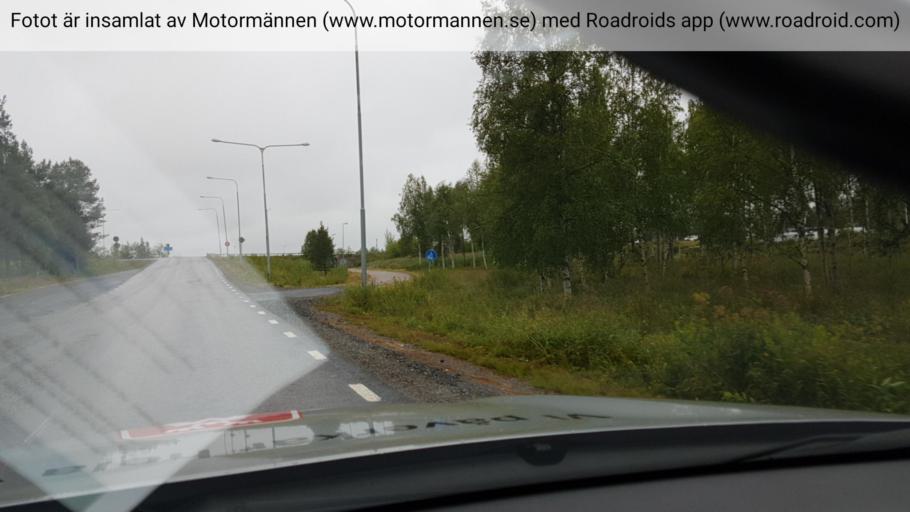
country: SE
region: Norrbotten
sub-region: Gallivare Kommun
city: Gaellivare
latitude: 67.1263
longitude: 20.6734
